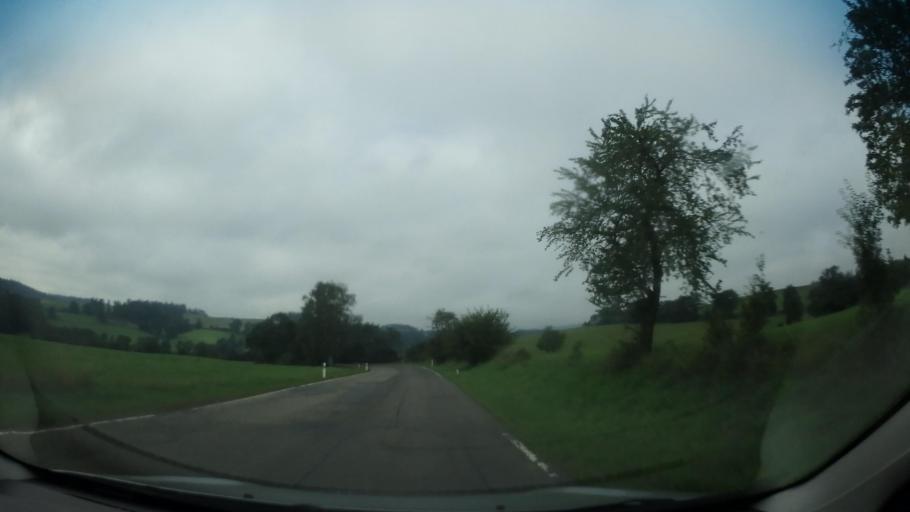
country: CZ
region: Central Bohemia
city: Neveklov
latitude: 49.7345
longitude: 14.4894
